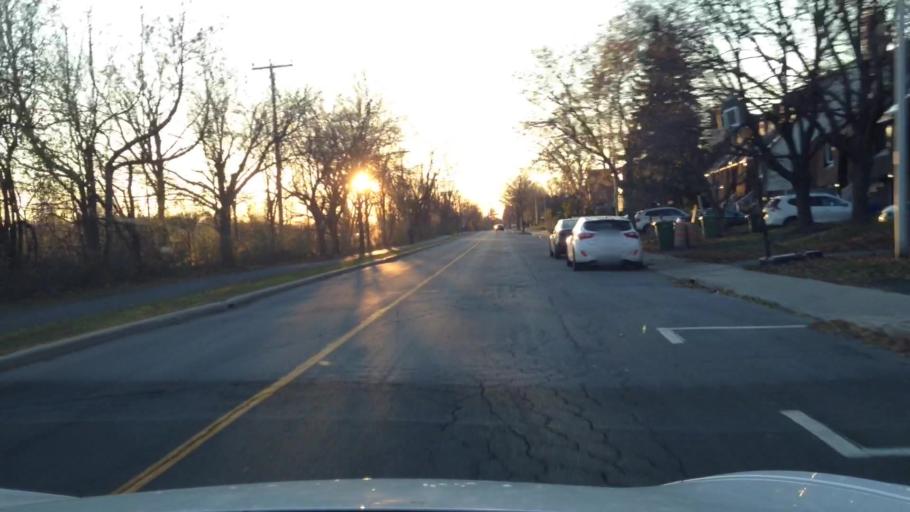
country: CA
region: Quebec
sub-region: Montreal
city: Pointe-Claire
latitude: 45.4376
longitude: -73.8384
